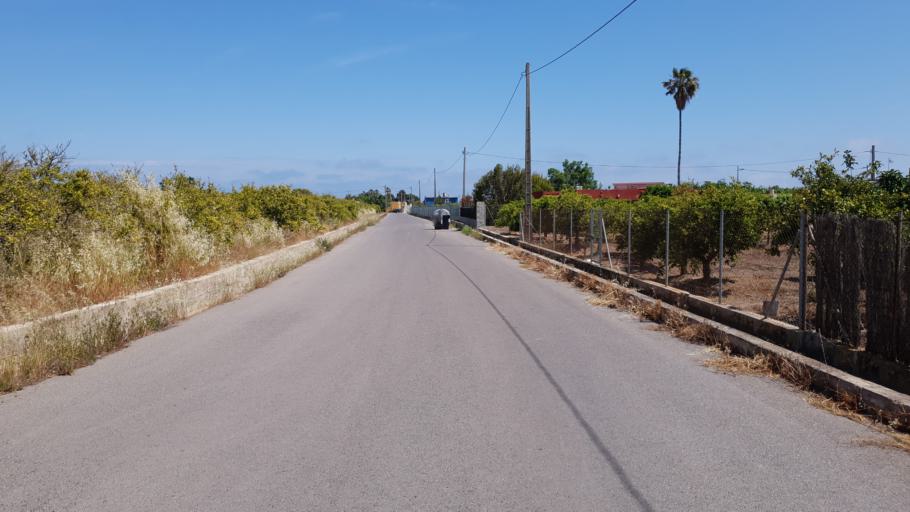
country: ES
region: Valencia
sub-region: Provincia de Castello
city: Burriana
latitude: 39.8607
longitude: -0.0899
